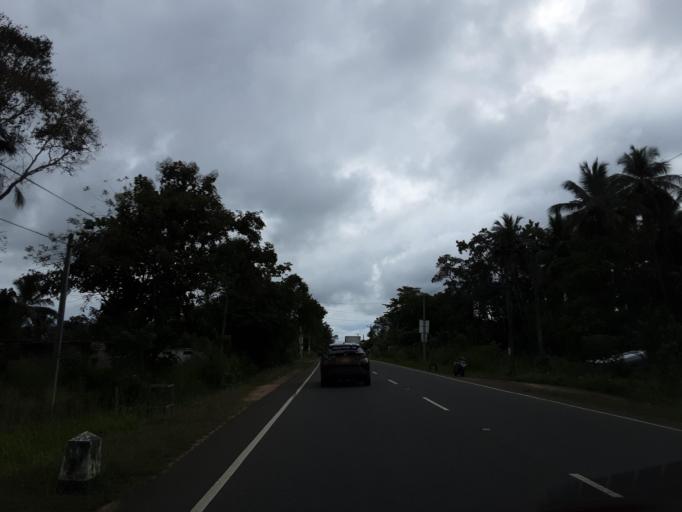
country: LK
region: Uva
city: Badulla
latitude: 7.3677
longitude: 81.0628
